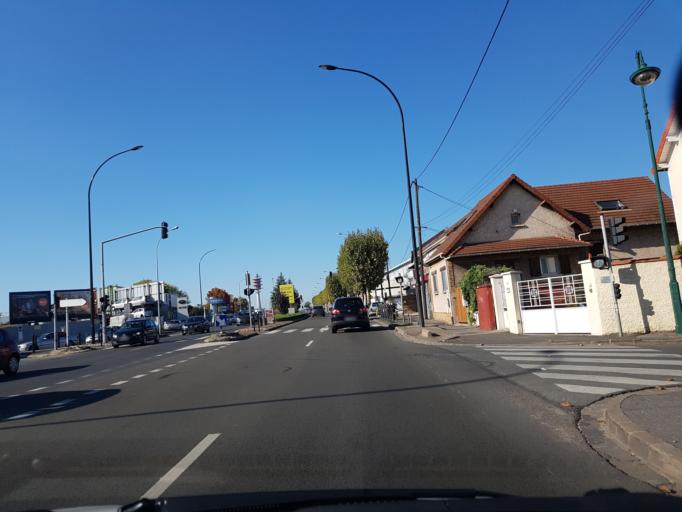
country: FR
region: Ile-de-France
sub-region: Departement du Val-de-Marne
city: Chennevieres-sur-Marne
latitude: 48.7968
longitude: 2.5486
